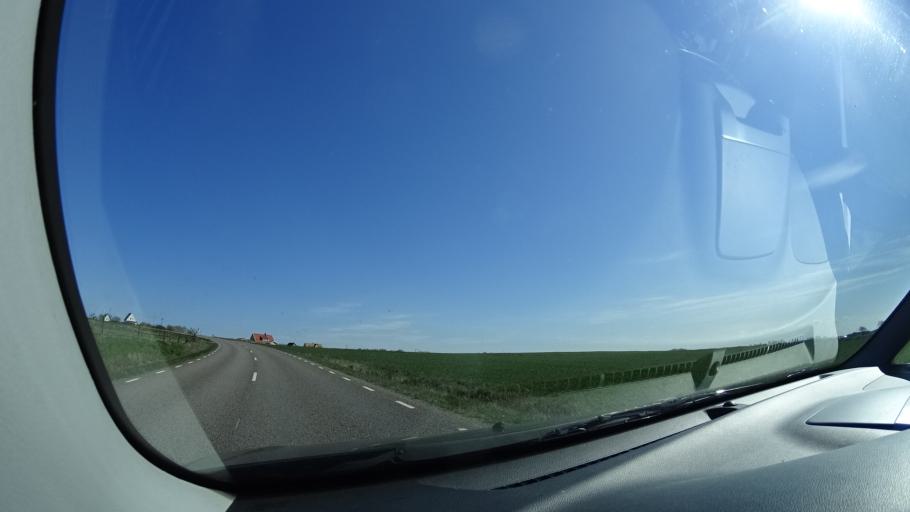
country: SE
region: Skane
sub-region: Hoganas Kommun
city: Hoganas
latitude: 56.2506
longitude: 12.5673
